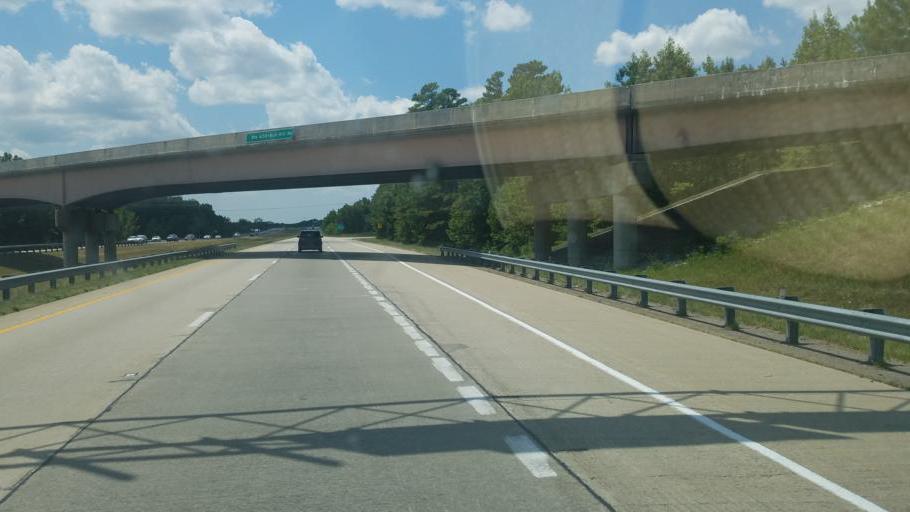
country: US
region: Virginia
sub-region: Prince George County
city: Prince George
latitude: 37.1968
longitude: -77.3200
